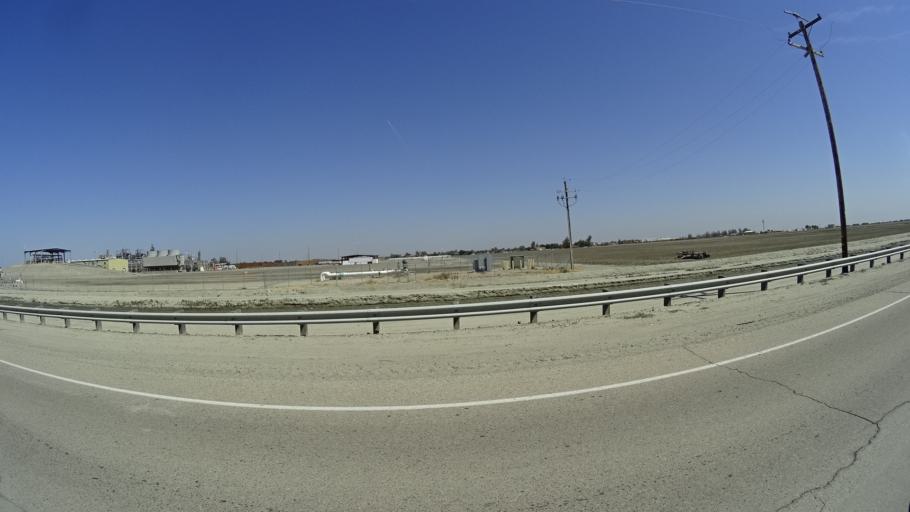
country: US
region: California
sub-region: Kings County
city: Corcoran
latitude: 36.0651
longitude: -119.5663
